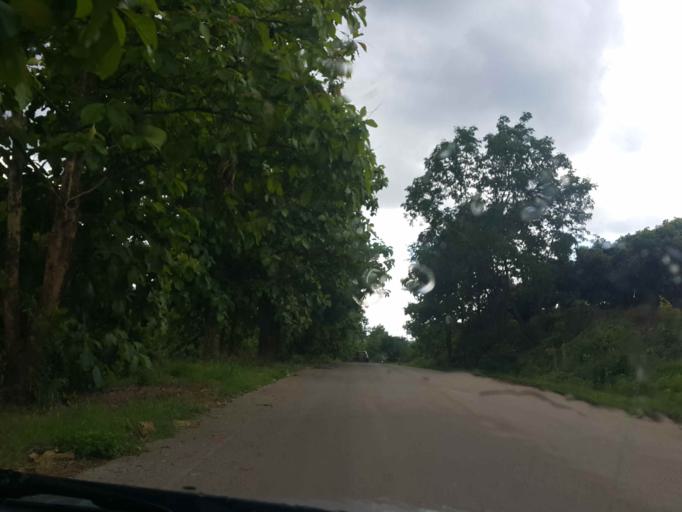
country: TH
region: Phayao
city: Dok Kham Tai
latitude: 18.9859
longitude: 100.0677
